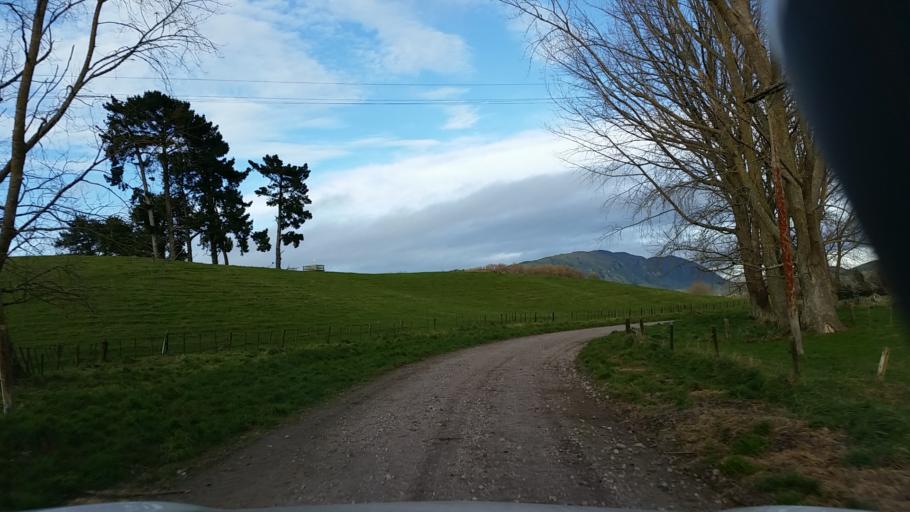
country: NZ
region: Bay of Plenty
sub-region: Rotorua District
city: Rotorua
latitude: -38.3163
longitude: 176.3017
